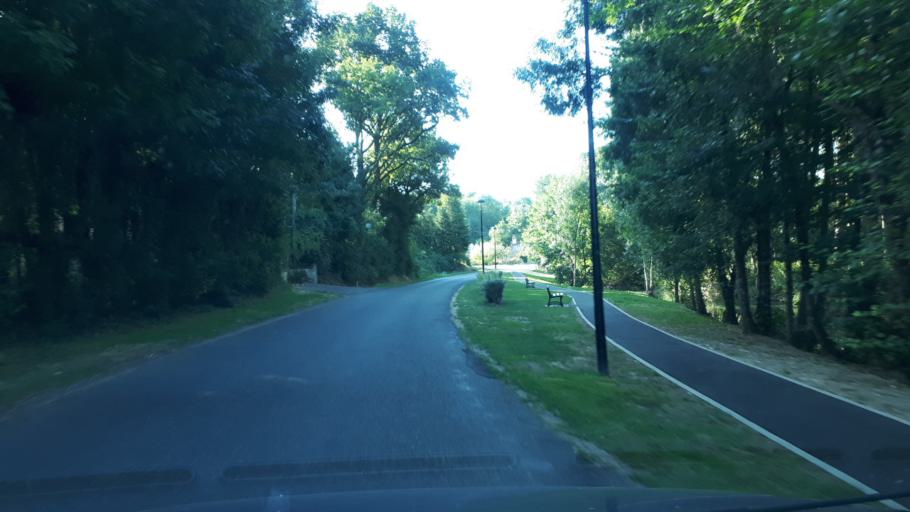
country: FR
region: Centre
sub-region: Departement d'Indre-et-Loire
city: Chateau-Renault
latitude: 47.6517
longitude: 0.9414
